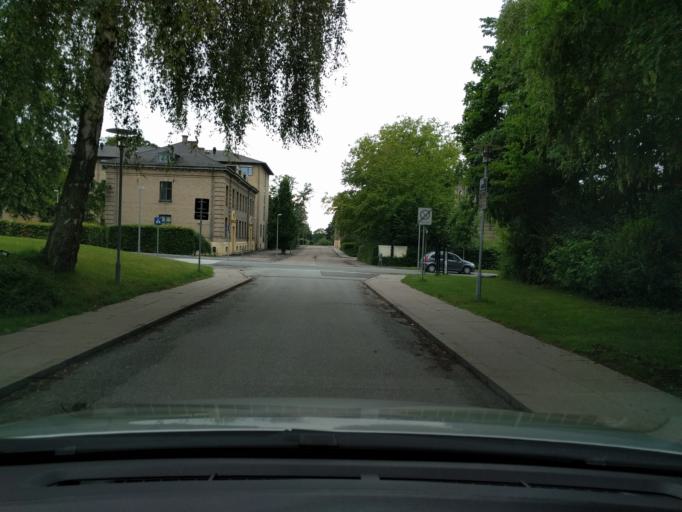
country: DK
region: Zealand
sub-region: Roskilde Kommune
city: Roskilde
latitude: 55.6507
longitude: 12.0700
